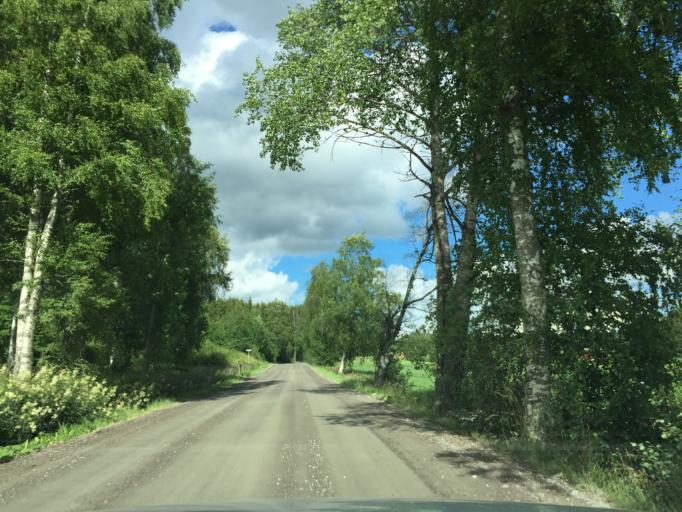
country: NO
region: Hedmark
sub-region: Kongsvinger
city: Spetalen
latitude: 60.2484
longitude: 11.8529
